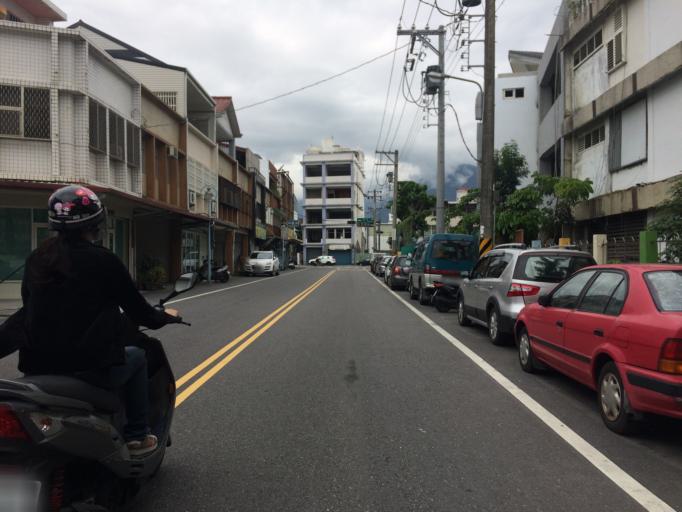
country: TW
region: Taiwan
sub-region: Hualien
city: Hualian
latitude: 23.9713
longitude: 121.5996
